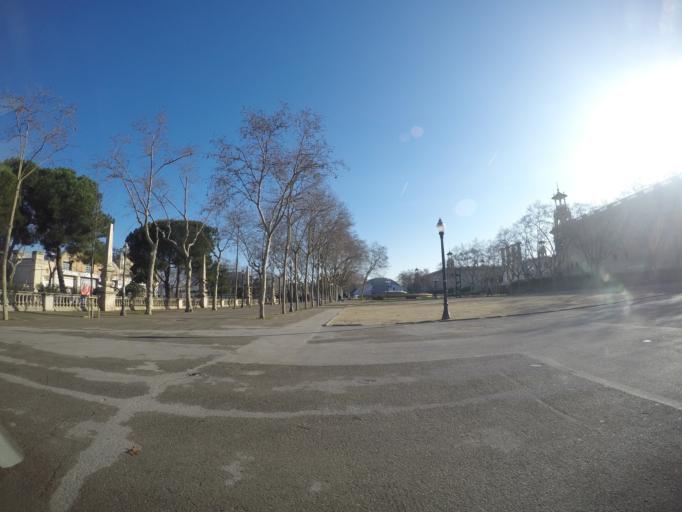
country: ES
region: Catalonia
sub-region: Provincia de Barcelona
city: Sants-Montjuic
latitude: 41.3707
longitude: 2.1501
